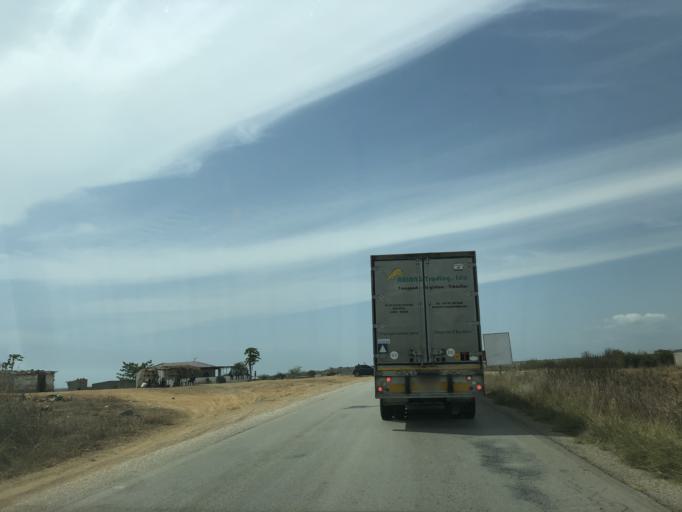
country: AO
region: Cuanza Sul
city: Sumbe
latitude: -10.6042
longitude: 13.7662
